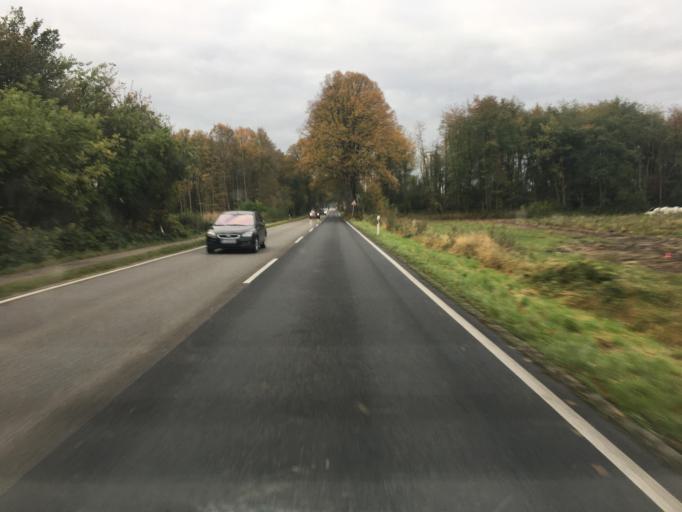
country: DE
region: North Rhine-Westphalia
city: Bruhl
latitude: 50.8707
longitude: 6.9319
